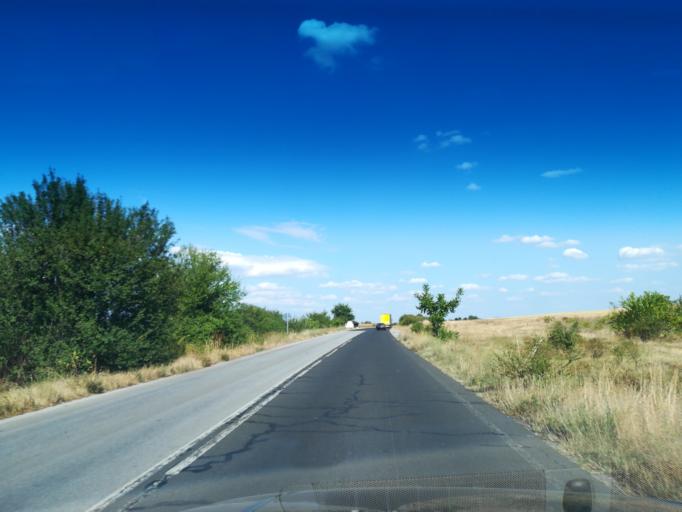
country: BG
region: Stara Zagora
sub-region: Obshtina Chirpan
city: Chirpan
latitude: 42.0590
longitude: 25.2782
